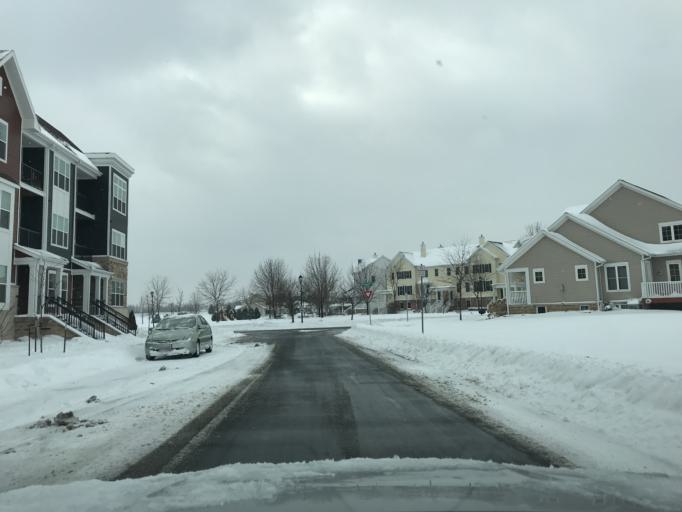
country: US
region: Wisconsin
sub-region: Dane County
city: Sun Prairie
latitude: 43.1677
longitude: -89.2789
